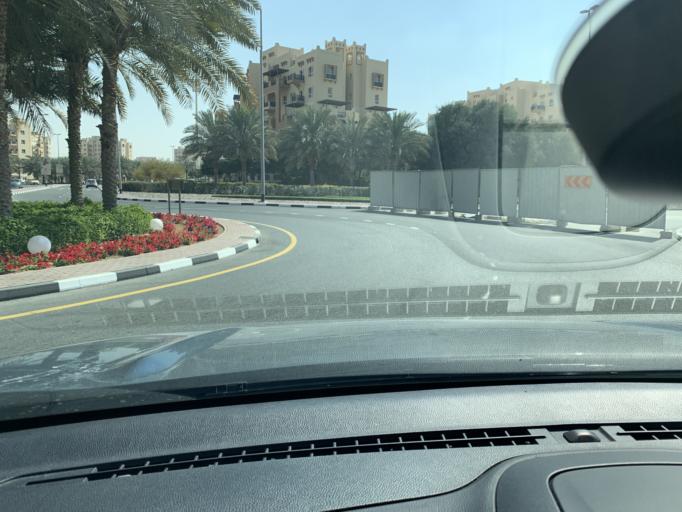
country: AE
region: Dubai
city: Dubai
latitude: 25.0050
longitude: 55.2510
